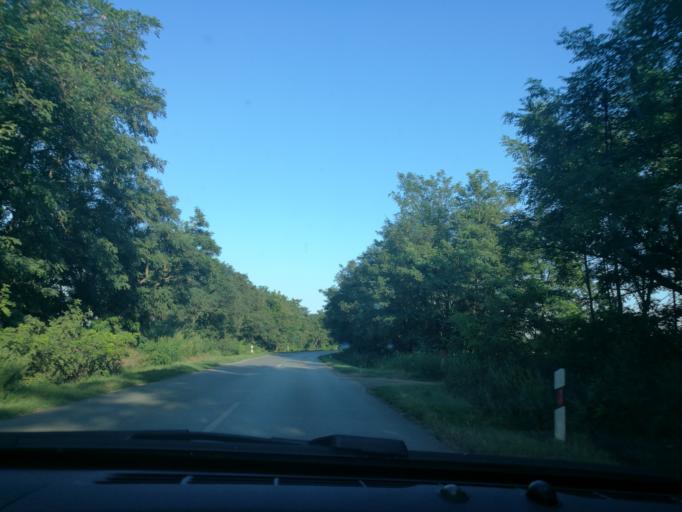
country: HU
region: Szabolcs-Szatmar-Bereg
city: Buj
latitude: 48.0583
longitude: 21.6588
